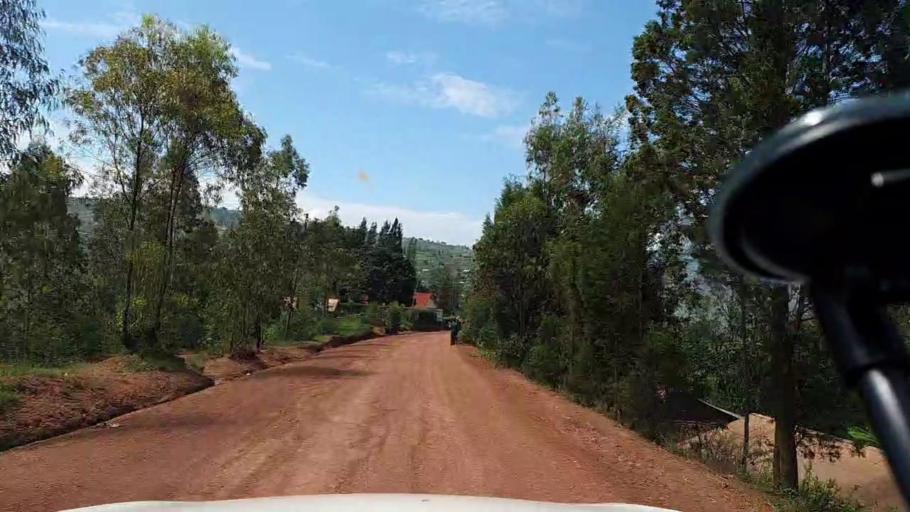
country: RW
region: Kigali
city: Kigali
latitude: -1.7991
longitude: 29.8963
